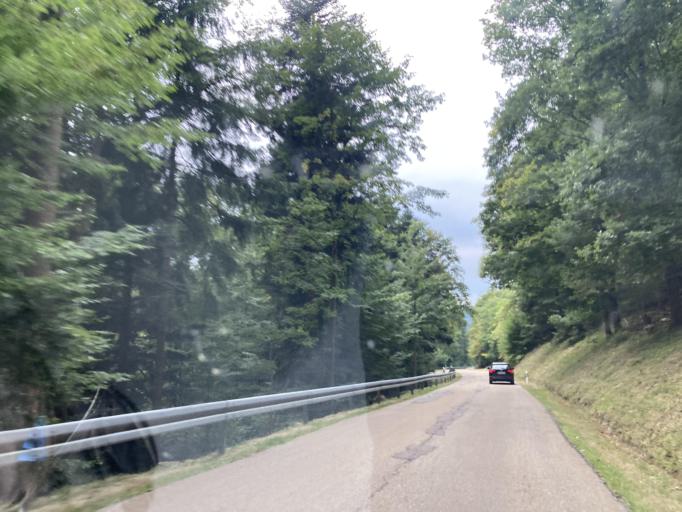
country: DE
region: Baden-Wuerttemberg
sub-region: Freiburg Region
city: Sulzburg
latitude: 47.8029
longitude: 7.7170
